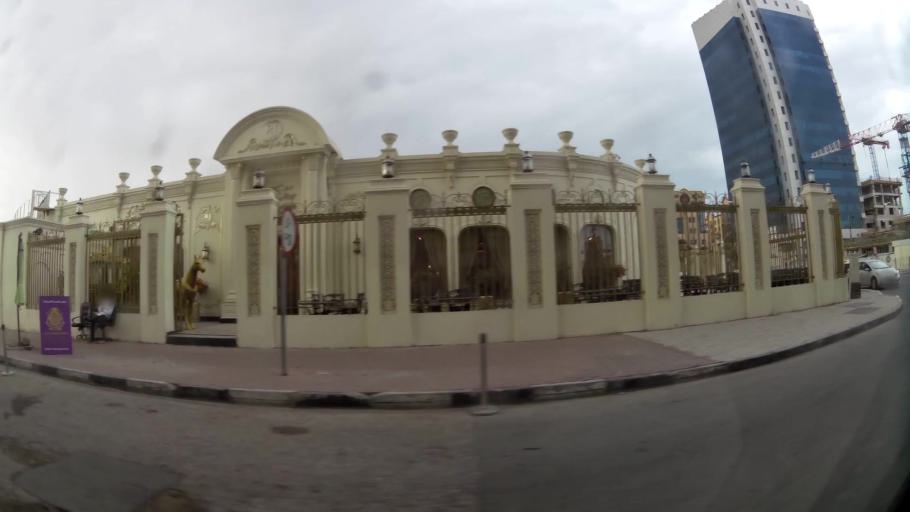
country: QA
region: Baladiyat ad Dawhah
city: Doha
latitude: 25.2737
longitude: 51.5092
